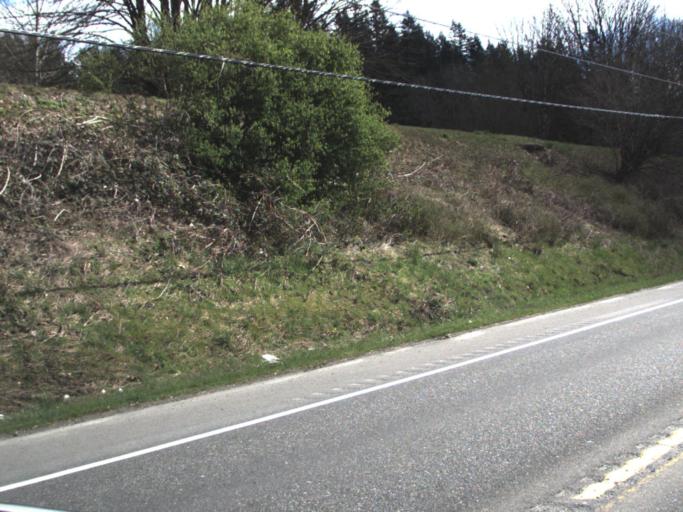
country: US
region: Washington
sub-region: King County
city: Maple Valley
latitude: 47.4122
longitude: -122.0410
